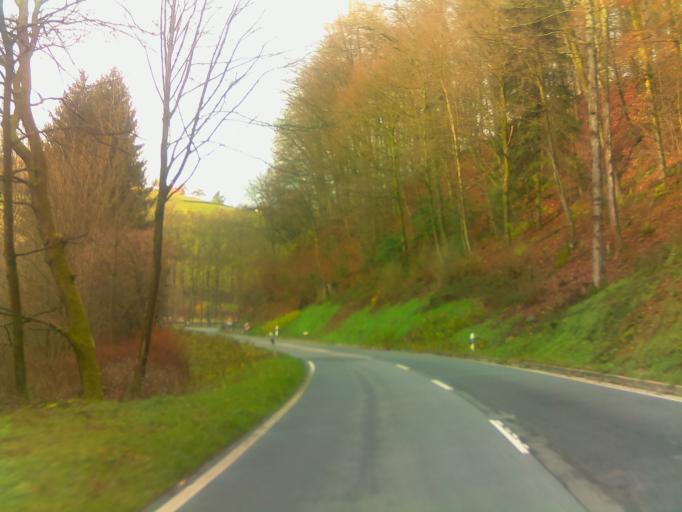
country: DE
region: Baden-Wuerttemberg
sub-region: Karlsruhe Region
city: Heiligkreuzsteinach
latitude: 49.4897
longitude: 8.7887
